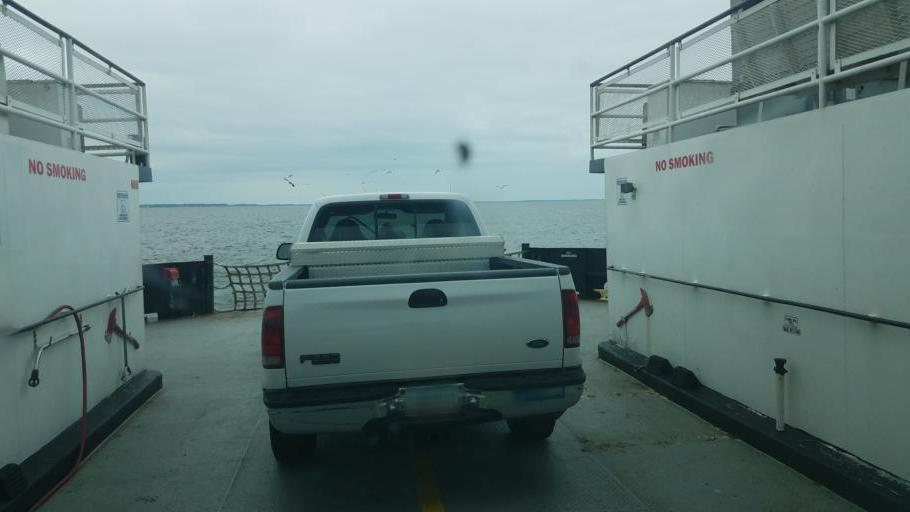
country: US
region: North Carolina
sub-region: Currituck County
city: Currituck
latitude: 36.4541
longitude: -75.9948
